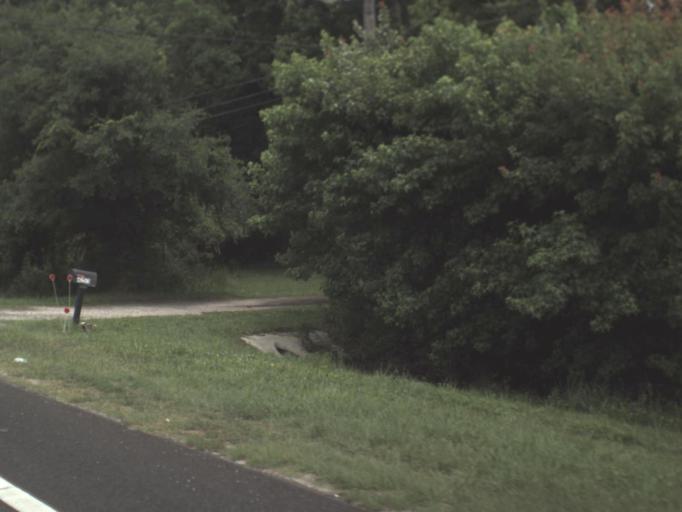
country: US
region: Florida
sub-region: Nassau County
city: Yulee
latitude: 30.6289
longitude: -81.6143
